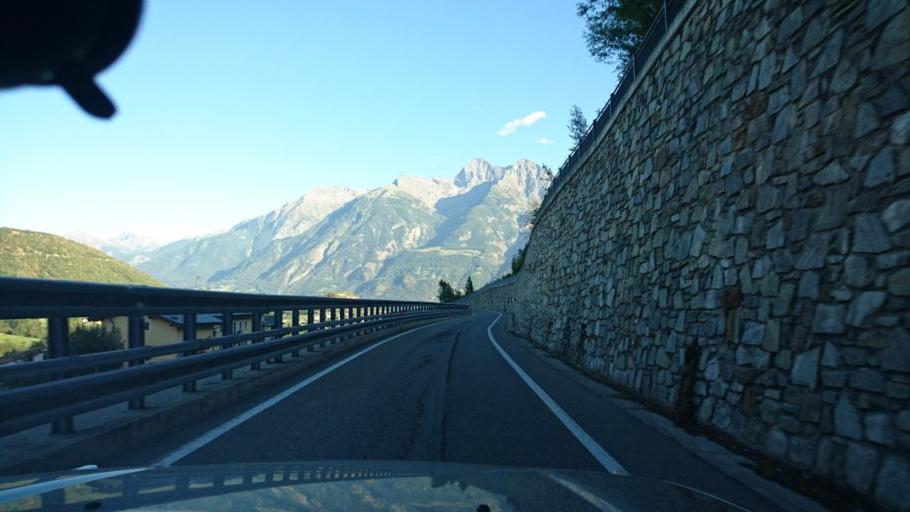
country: IT
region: Aosta Valley
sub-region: Valle d'Aosta
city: La Cretaz-Roisan
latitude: 45.7636
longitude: 7.3129
